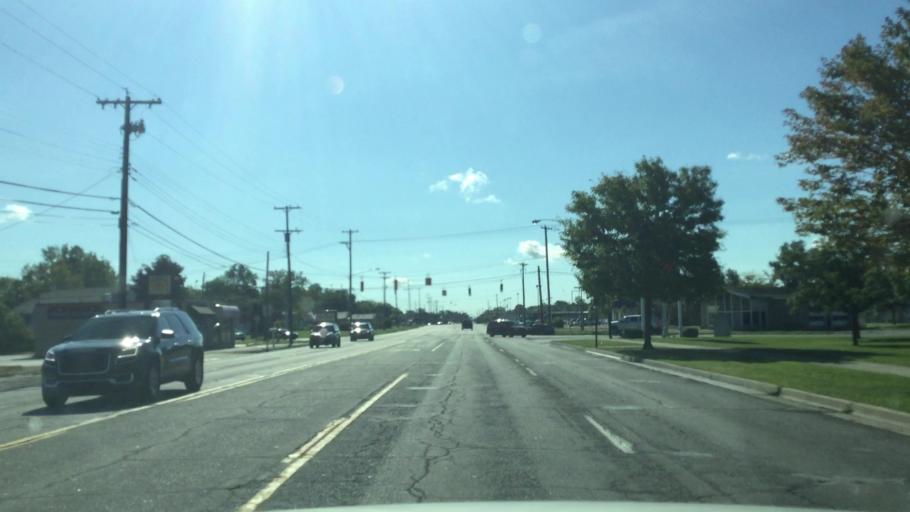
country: US
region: Michigan
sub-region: Genesee County
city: Grand Blanc
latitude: 42.9607
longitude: -83.6683
